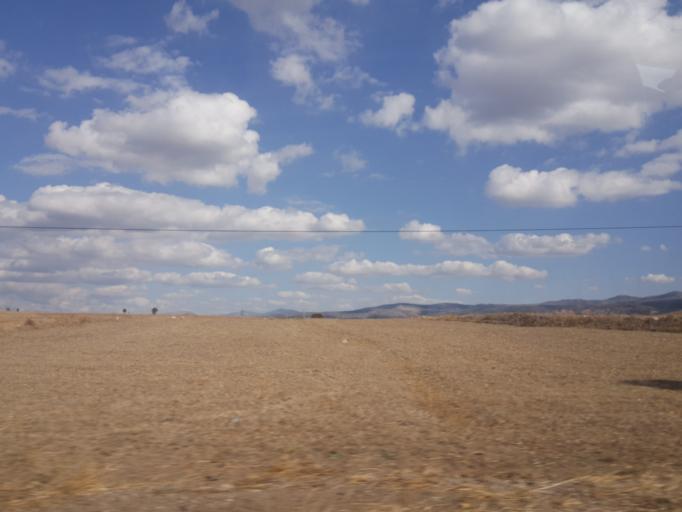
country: TR
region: Tokat
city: Artova
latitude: 40.0487
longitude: 36.3009
